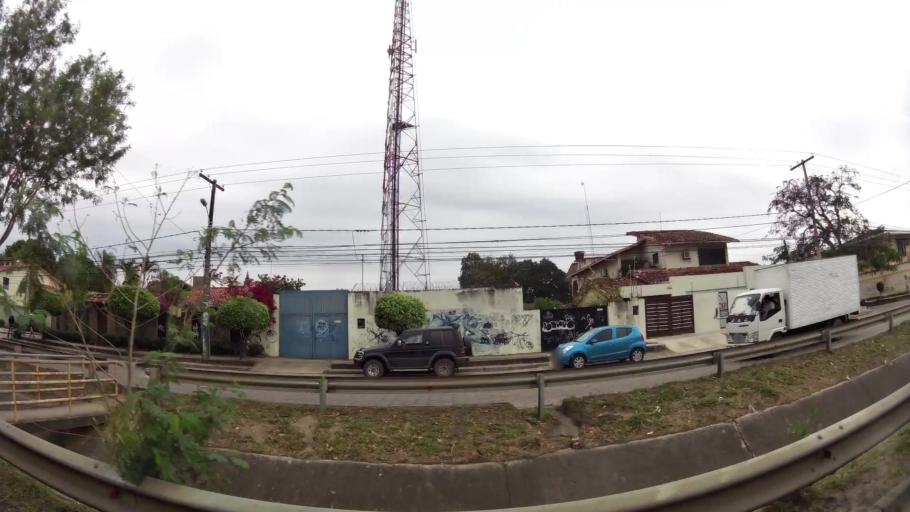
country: BO
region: Santa Cruz
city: Santa Cruz de la Sierra
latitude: -17.7536
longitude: -63.1815
